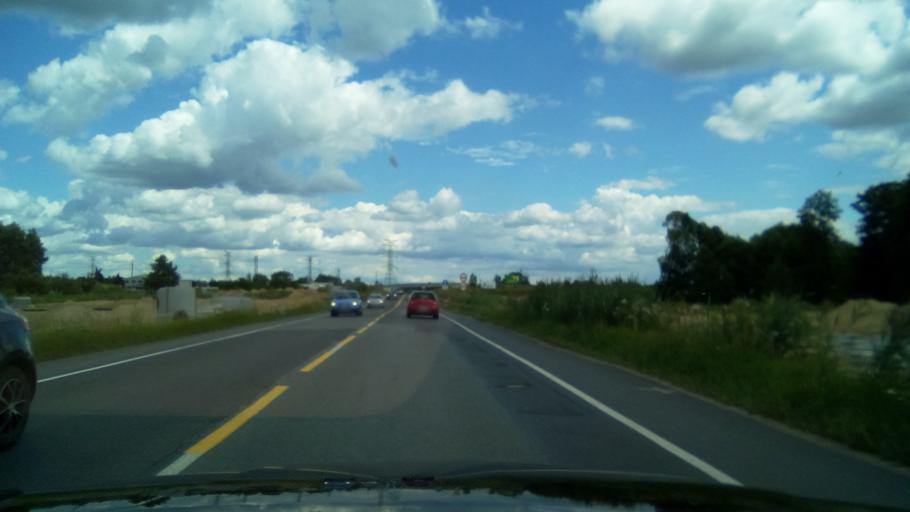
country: PL
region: Kujawsko-Pomorskie
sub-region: Powiat bydgoski
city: Biale Blota
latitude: 53.0819
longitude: 17.8656
